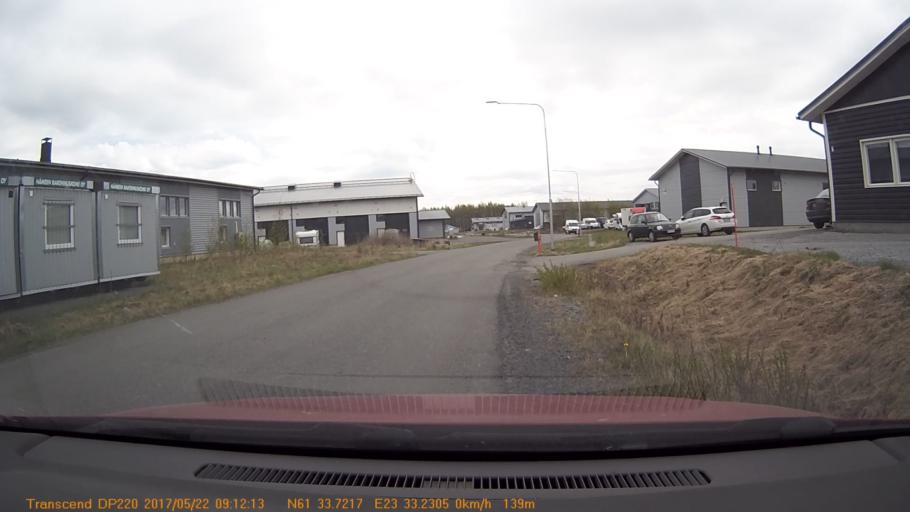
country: FI
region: Pirkanmaa
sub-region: Tampere
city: Yloejaervi
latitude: 61.5620
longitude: 23.5538
